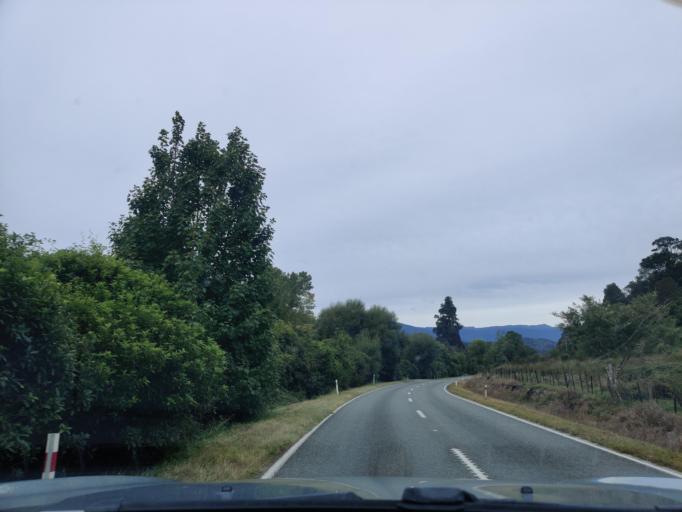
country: NZ
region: West Coast
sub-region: Buller District
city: Westport
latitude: -41.8420
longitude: 171.9359
